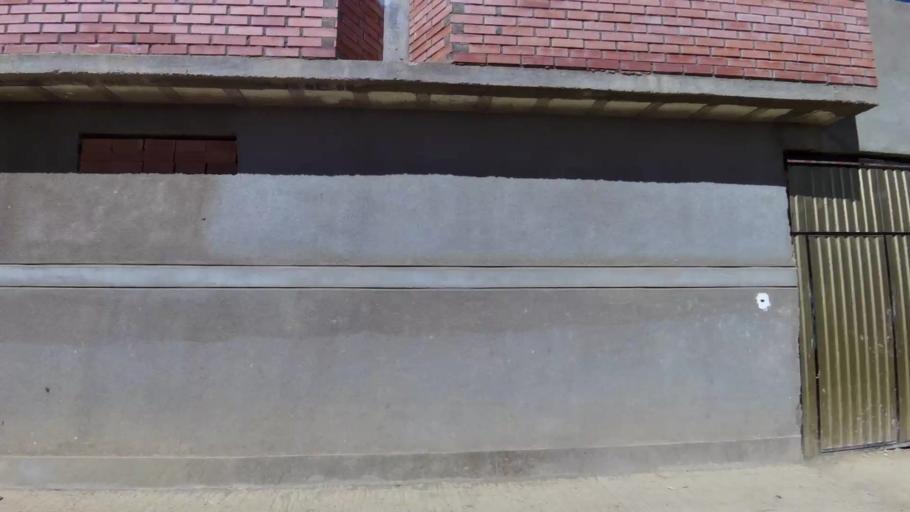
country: BO
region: La Paz
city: La Paz
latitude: -16.5727
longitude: -68.2213
